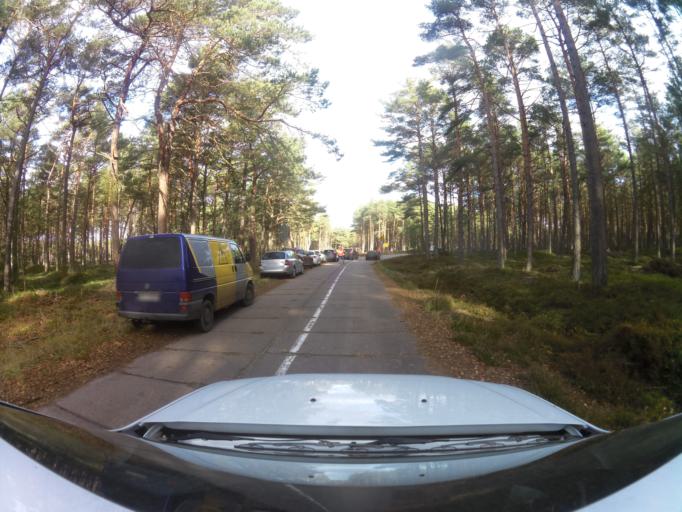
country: PL
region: West Pomeranian Voivodeship
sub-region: Powiat gryficki
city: Cerkwica
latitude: 54.1086
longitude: 15.1485
